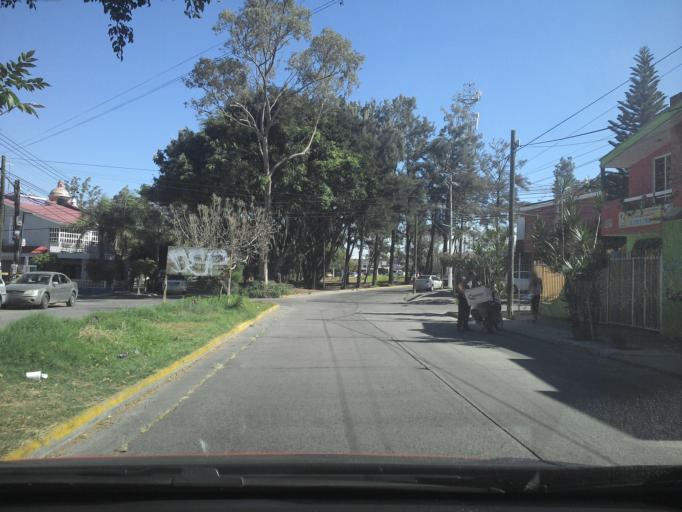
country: MX
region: Jalisco
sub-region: Zapopan
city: Zapopan
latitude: 20.7471
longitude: -103.4039
